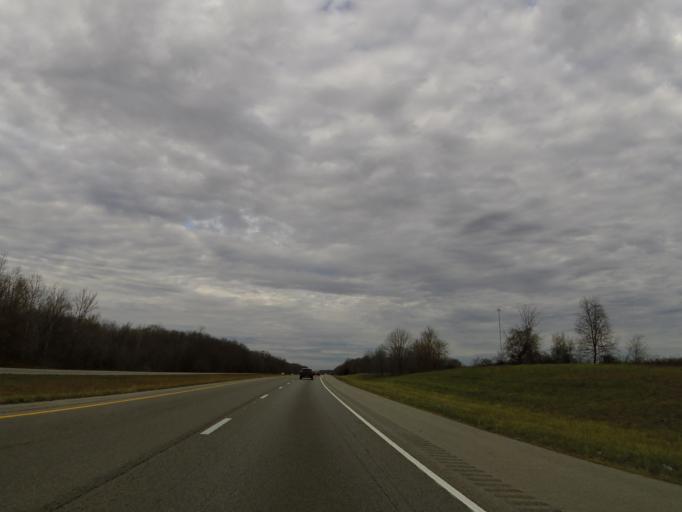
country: US
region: Illinois
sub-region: Clinton County
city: Wamac
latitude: 38.3651
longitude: -89.0860
